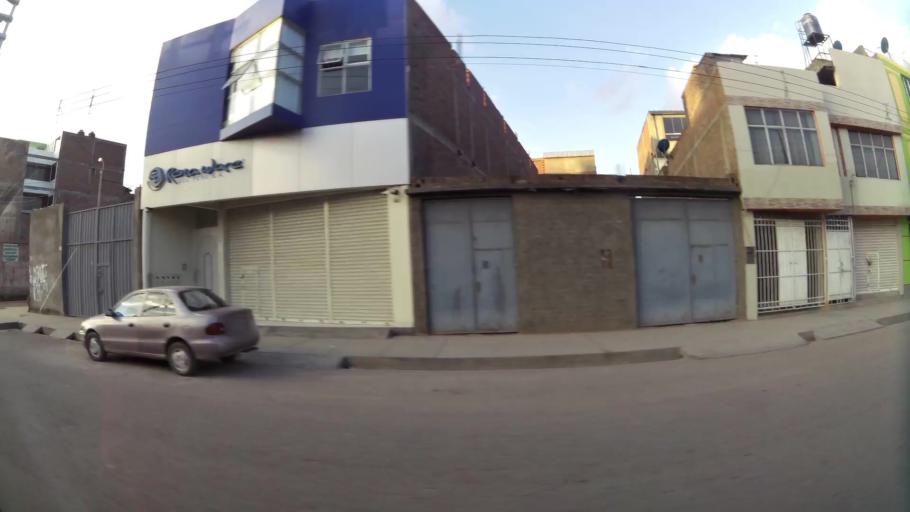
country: PE
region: Junin
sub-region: Provincia de Huancayo
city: El Tambo
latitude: -12.0496
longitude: -75.2285
